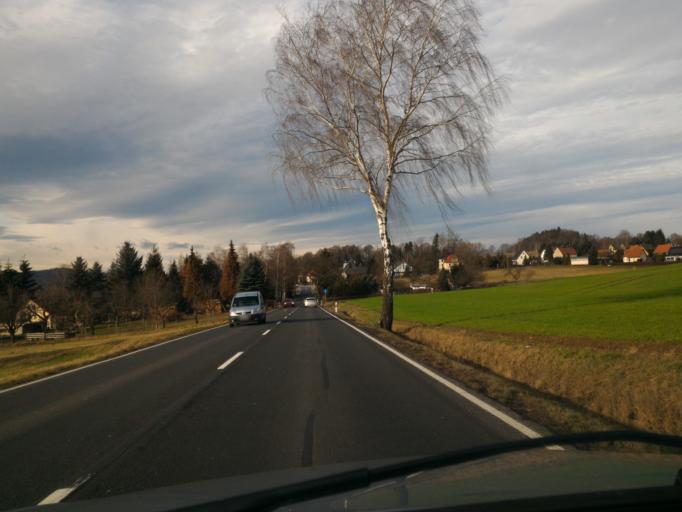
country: DE
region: Saxony
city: Demitz-Thumitz
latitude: 51.0994
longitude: 14.2458
